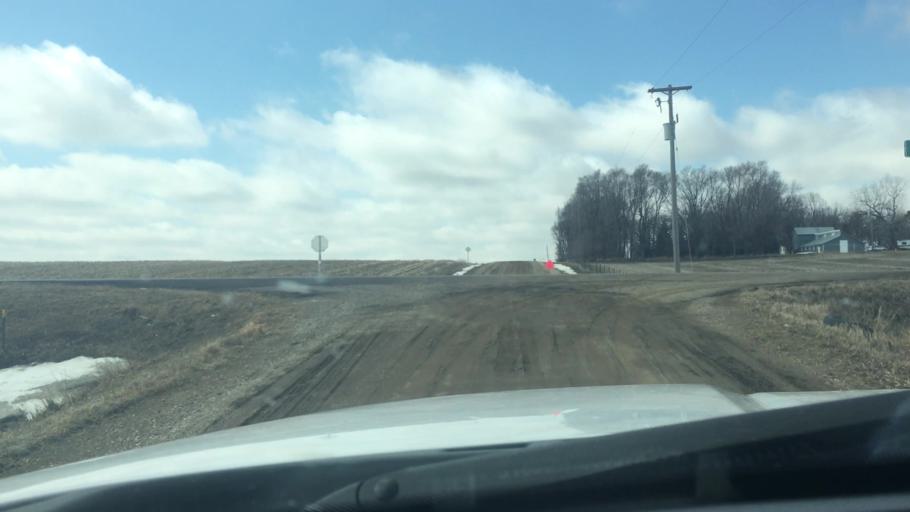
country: US
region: South Dakota
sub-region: Minnehaha County
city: Crooks
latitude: 43.6163
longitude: -96.8107
